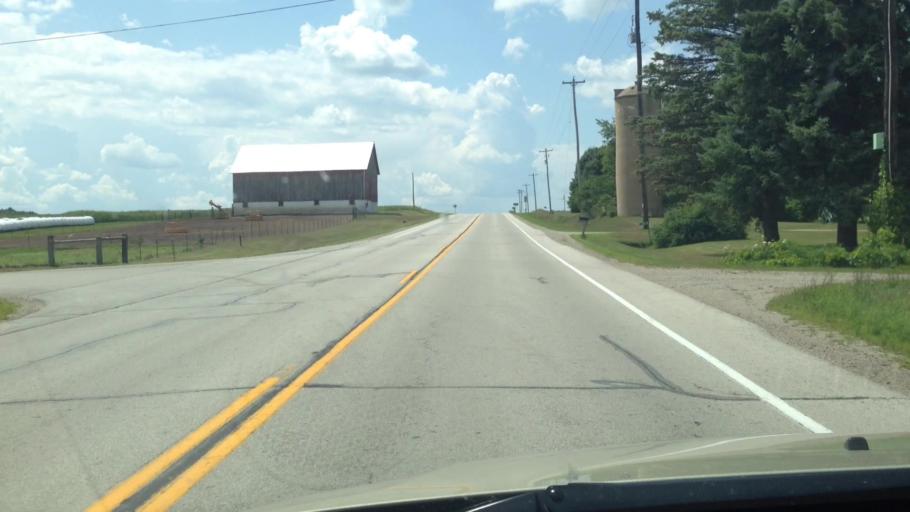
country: US
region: Wisconsin
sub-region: Brown County
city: Pulaski
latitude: 44.6470
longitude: -88.1451
